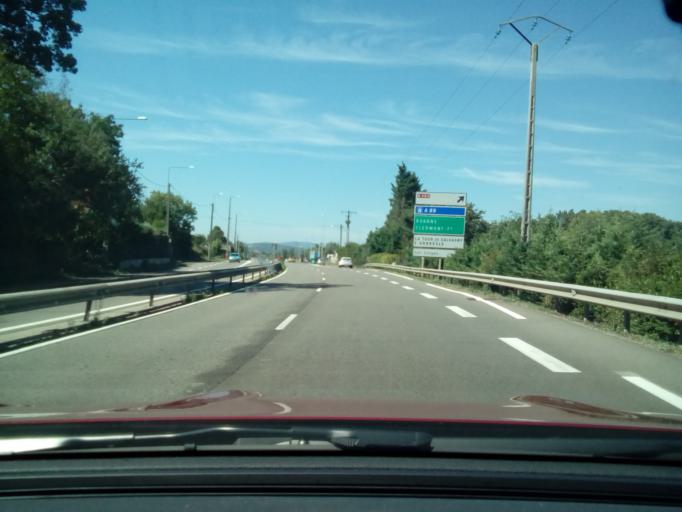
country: FR
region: Rhone-Alpes
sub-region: Departement du Rhone
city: Limonest
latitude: 45.8317
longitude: 4.7517
